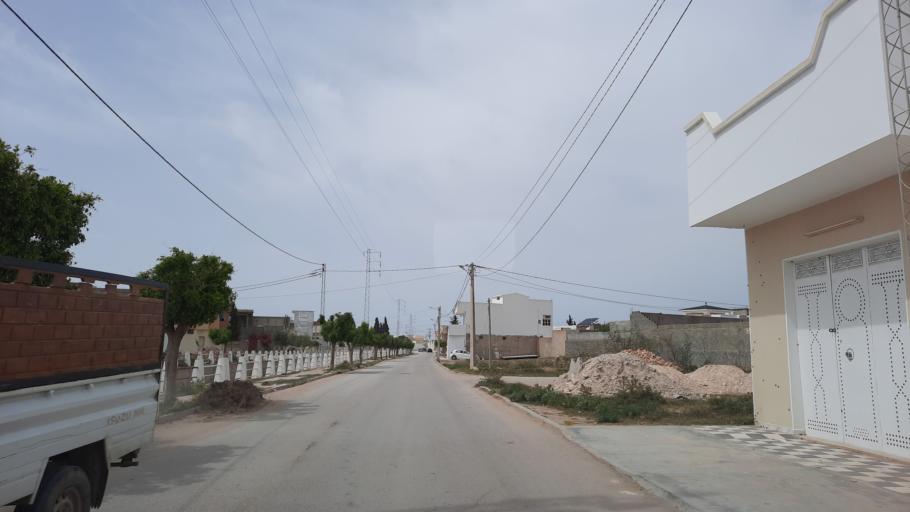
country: TN
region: Al Mahdiyah
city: El Jem
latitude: 35.3040
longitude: 10.7046
